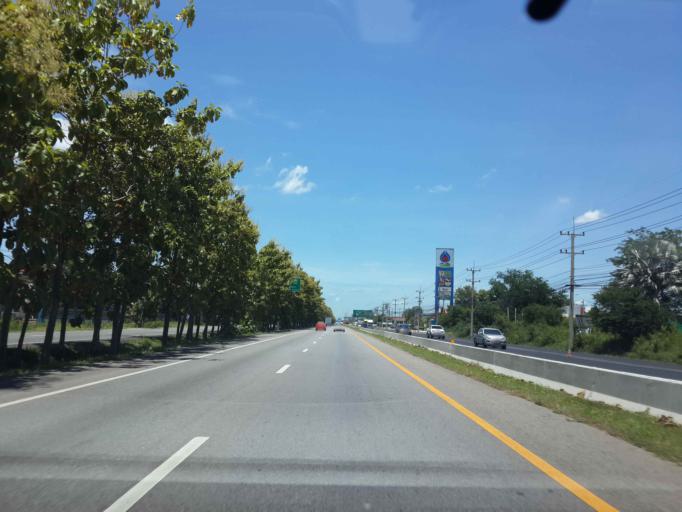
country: TH
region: Phetchaburi
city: Khao Yoi
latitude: 13.3030
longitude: 99.8245
